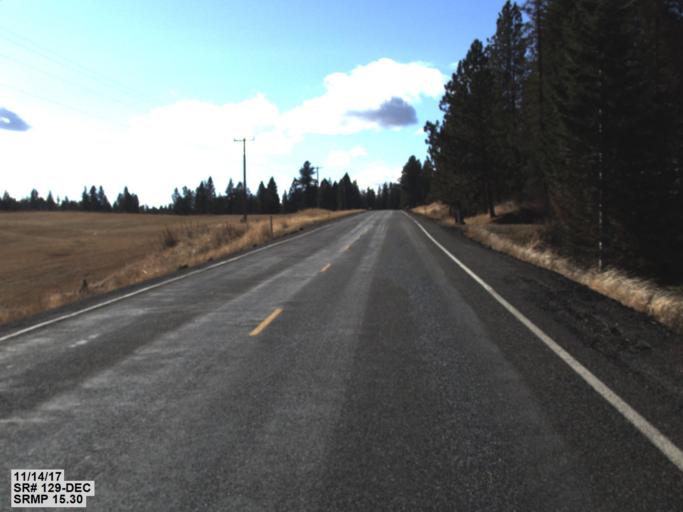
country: US
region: Washington
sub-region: Asotin County
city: Asotin
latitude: 46.1044
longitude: -117.1415
